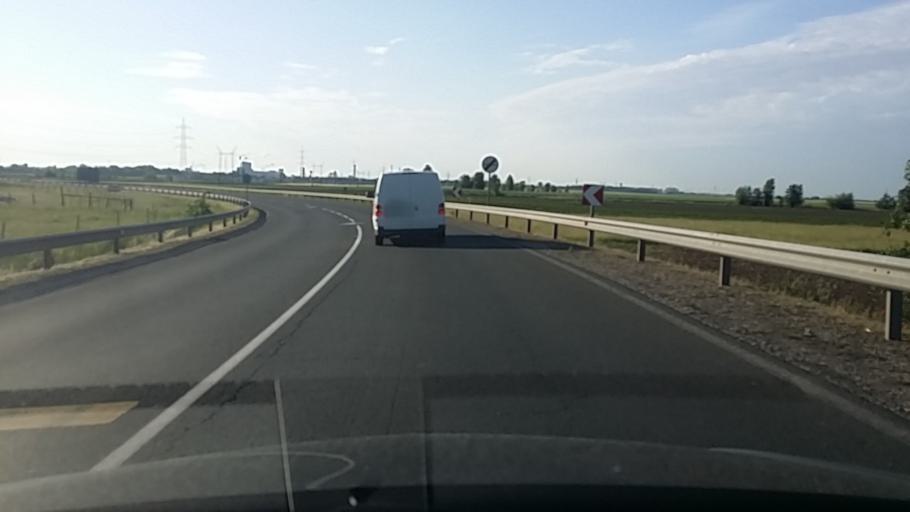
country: HU
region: Fejer
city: dunaujvaros
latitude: 46.9669
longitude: 18.8938
